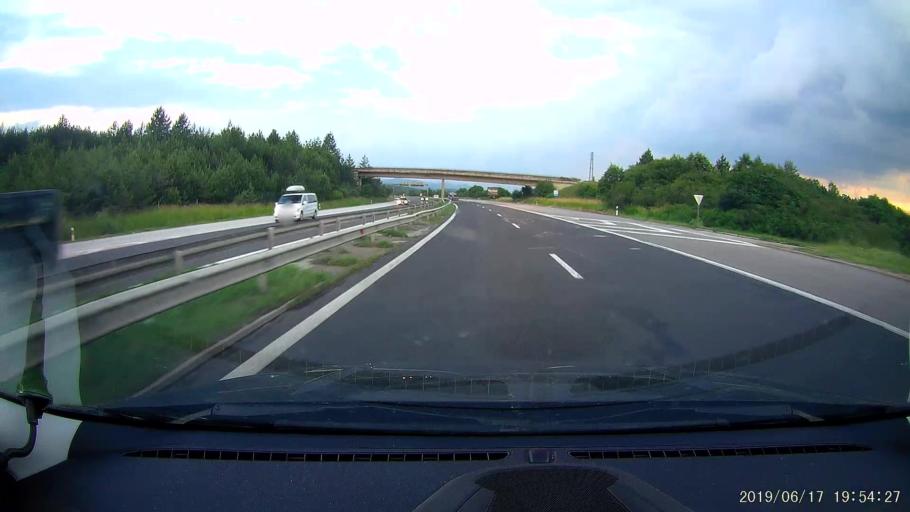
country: BG
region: Sofiya
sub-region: Obshtina Gorna Malina
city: Gorna Malina
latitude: 42.5537
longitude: 23.6946
